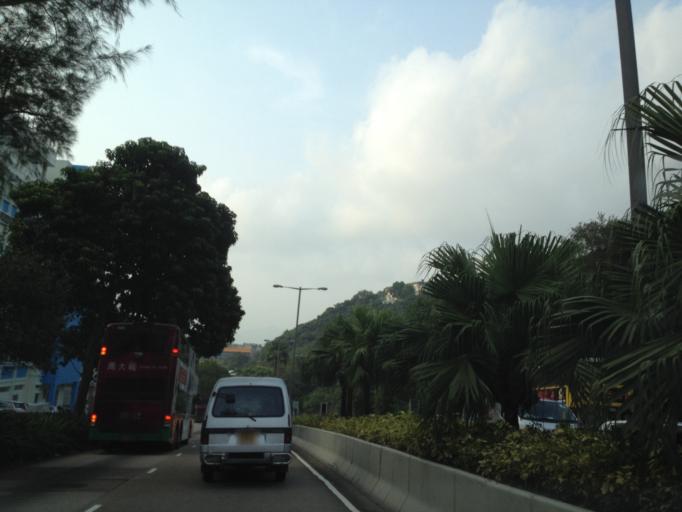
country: HK
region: Wanchai
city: Wan Chai
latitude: 22.2714
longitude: 114.2330
